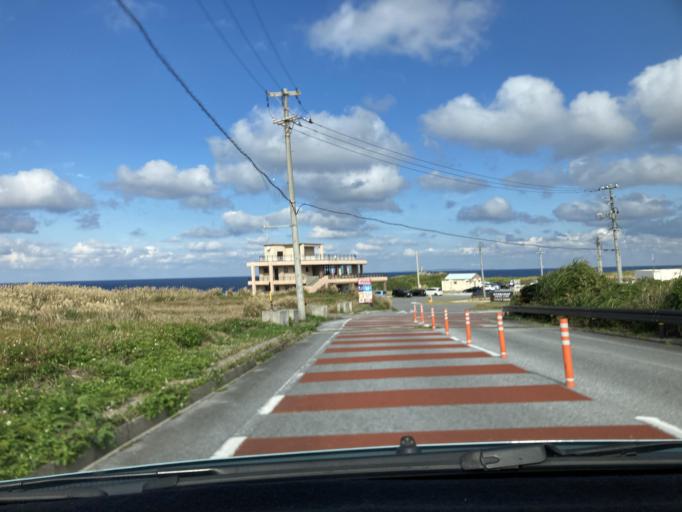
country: JP
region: Okinawa
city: Nago
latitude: 26.8717
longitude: 128.2627
